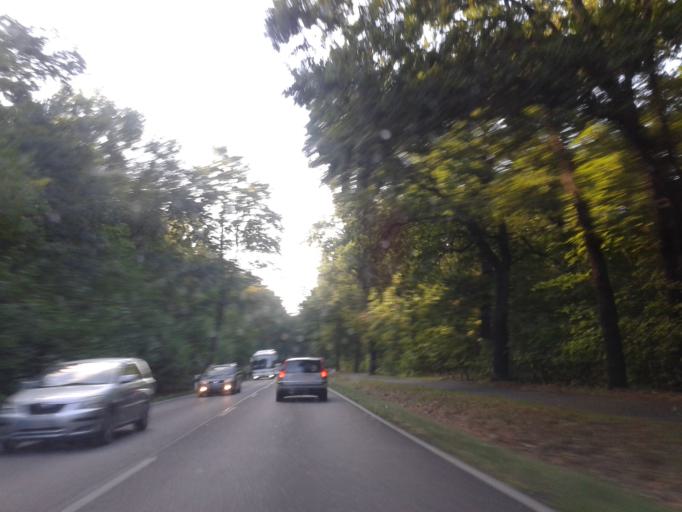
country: DE
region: Saxony
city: Radebeul
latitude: 51.1067
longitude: 13.7081
